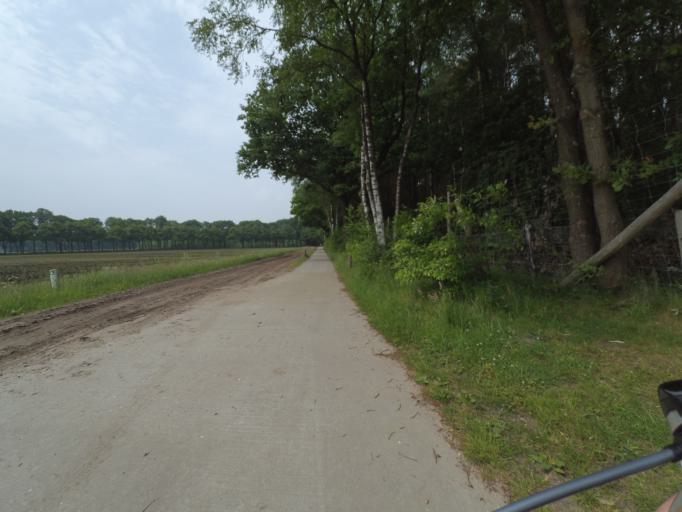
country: NL
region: Gelderland
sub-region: Gemeente Ede
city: Wekerom
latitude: 52.0525
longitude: 5.7268
